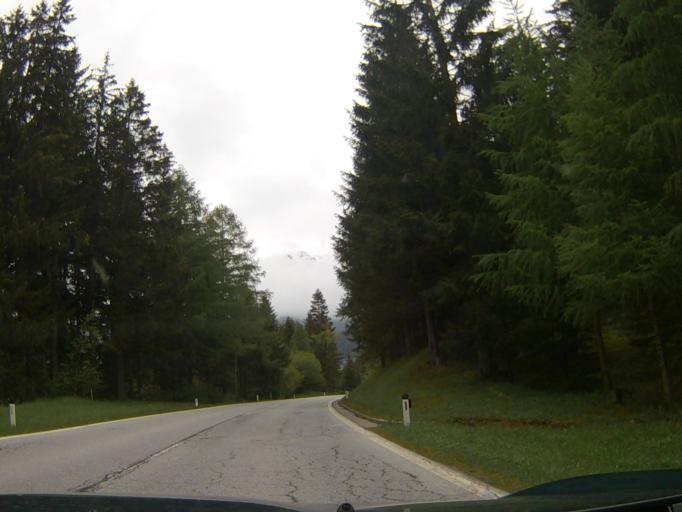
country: AT
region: Carinthia
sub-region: Politischer Bezirk Spittal an der Drau
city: Obervellach
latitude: 46.9531
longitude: 13.1831
